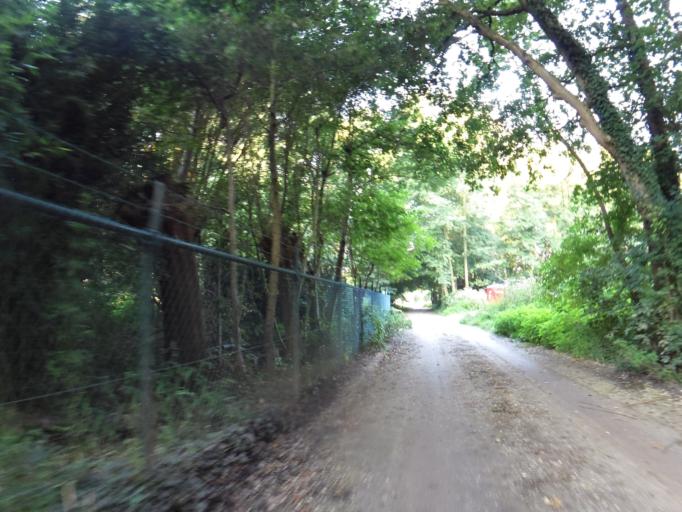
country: NL
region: Limburg
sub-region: Gemeente Onderbanken
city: Schinveld
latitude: 50.9701
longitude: 5.9902
